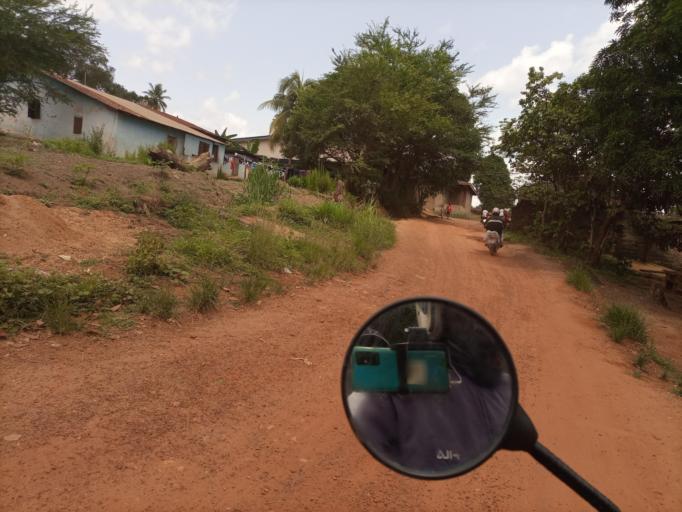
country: SL
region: Southern Province
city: Bo
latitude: 7.9521
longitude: -11.7357
